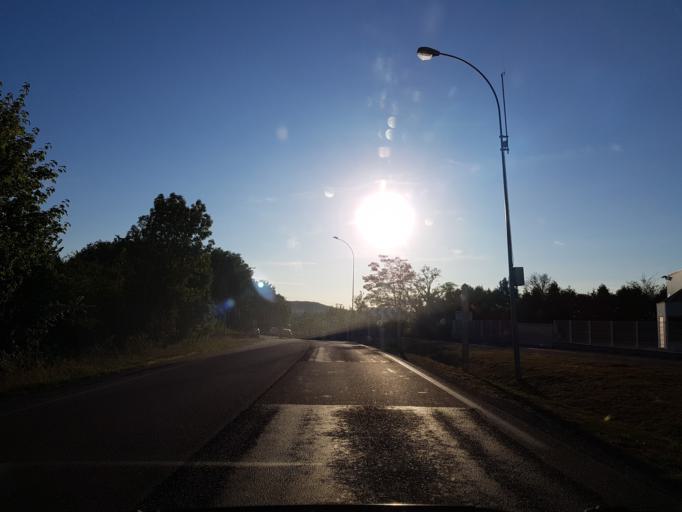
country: FR
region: Franche-Comte
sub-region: Departement de la Haute-Saone
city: Port-sur-Saone
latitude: 47.6874
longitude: 6.0575
